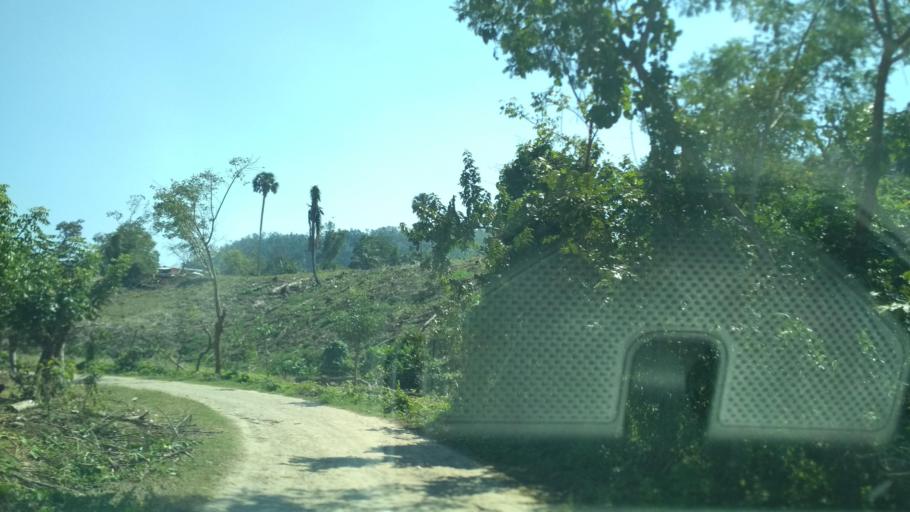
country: MX
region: Veracruz
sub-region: Papantla
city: Polutla
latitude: 20.4824
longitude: -97.2262
